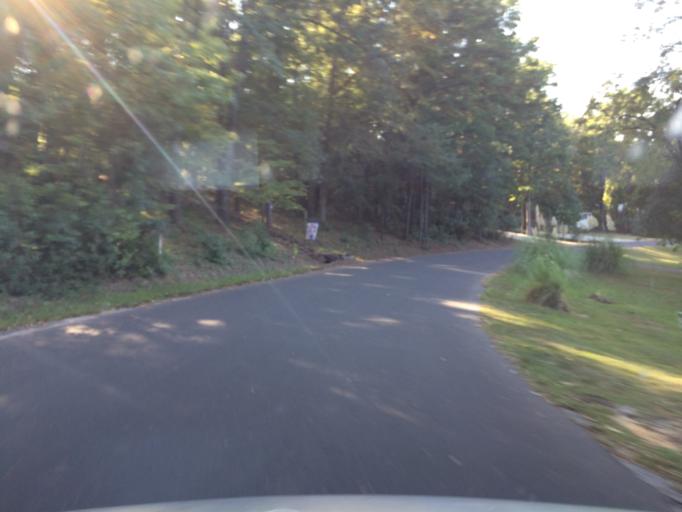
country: US
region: Texas
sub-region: Wood County
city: Hawkins
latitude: 32.6264
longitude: -95.2558
